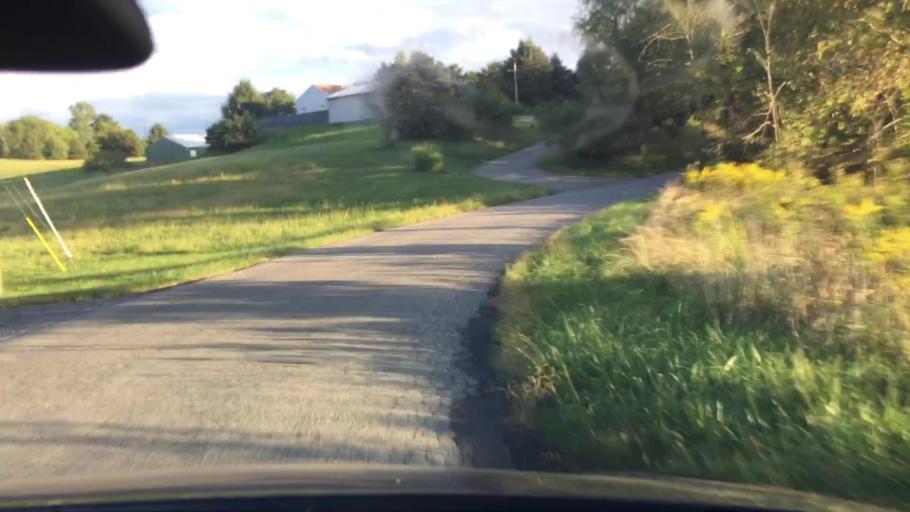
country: US
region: Pennsylvania
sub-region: Butler County
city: Nixon
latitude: 40.7422
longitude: -79.8805
